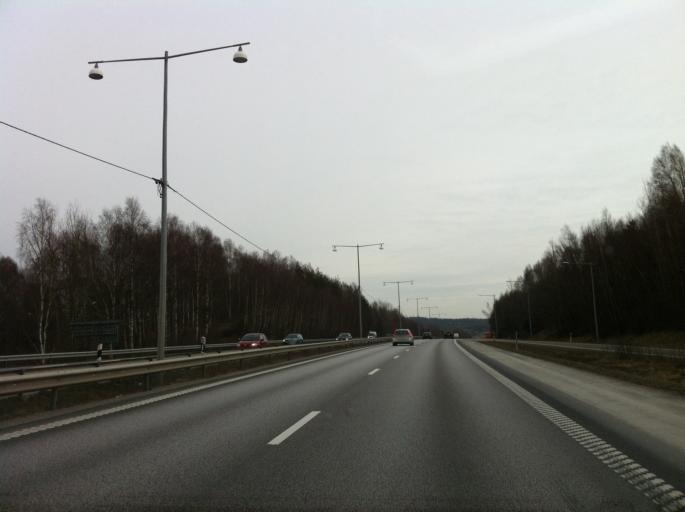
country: SE
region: Vaestra Goetaland
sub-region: Kungalvs Kommun
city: Kungalv
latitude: 57.8981
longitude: 11.9243
